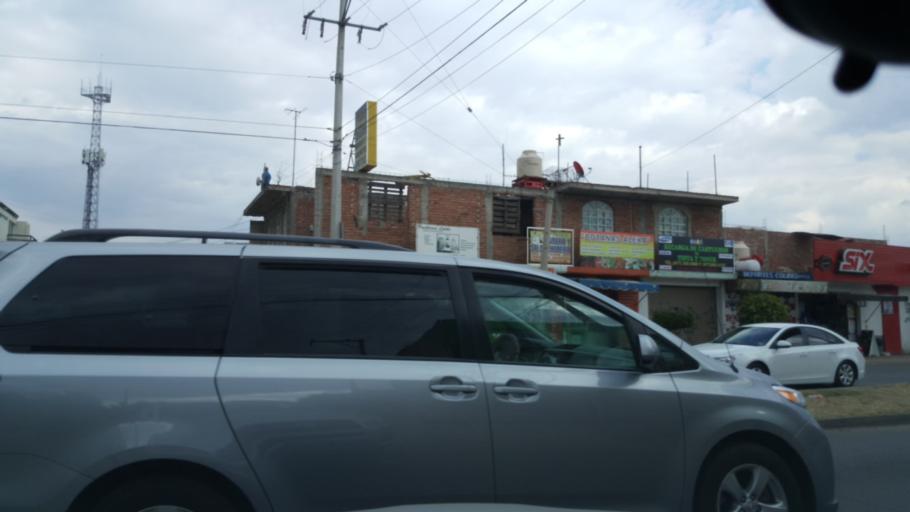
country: MX
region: Guanajuato
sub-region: Leon
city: Fraccionamiento Paraiso Real
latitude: 21.1005
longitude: -101.6111
